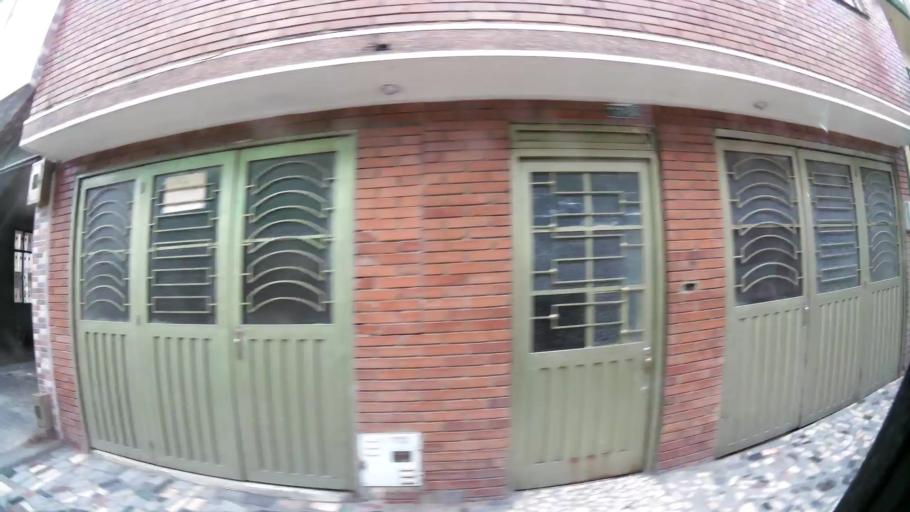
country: CO
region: Cundinamarca
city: Funza
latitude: 4.7029
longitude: -74.1338
